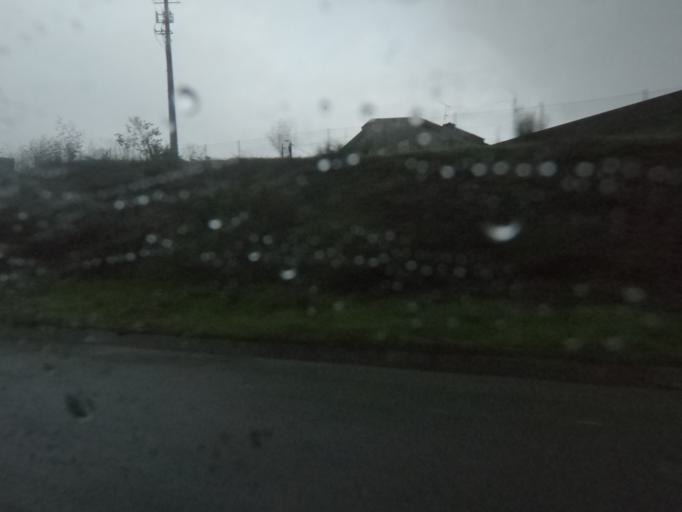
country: PT
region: Braga
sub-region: Braga
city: Braga
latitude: 41.5319
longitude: -8.4522
